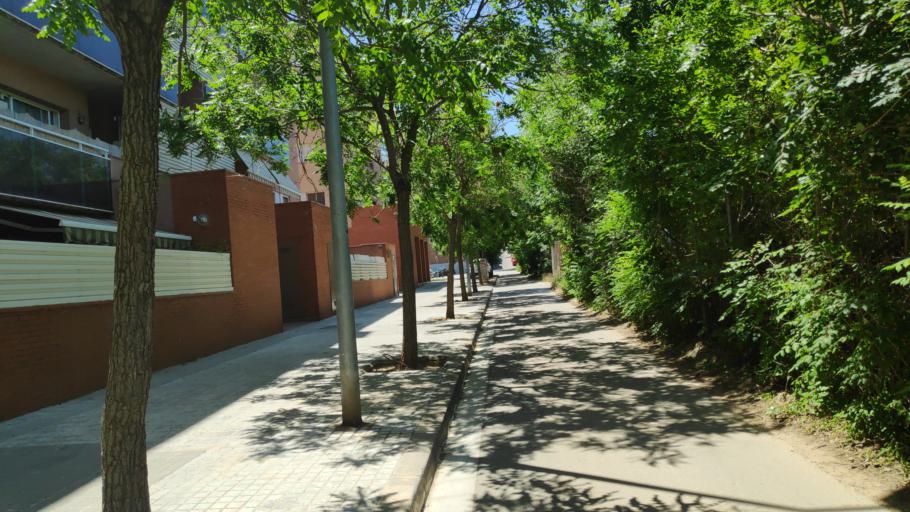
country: ES
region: Catalonia
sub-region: Provincia de Barcelona
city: Sant Quirze del Valles
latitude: 41.5533
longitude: 2.0815
